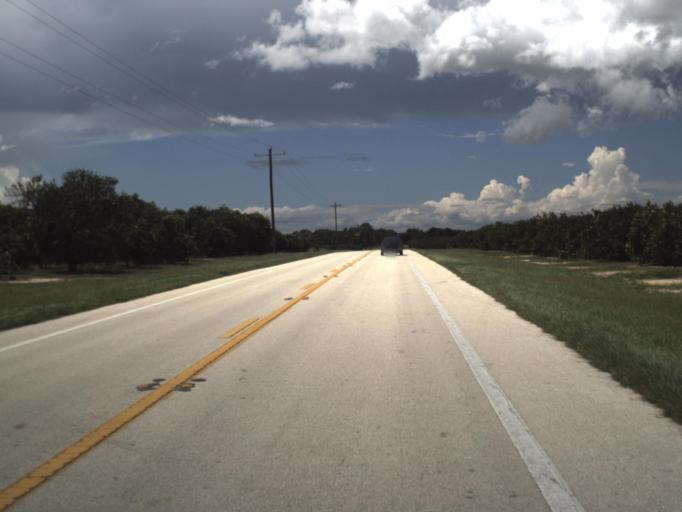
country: US
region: Florida
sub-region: Polk County
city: Fort Meade
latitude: 27.7335
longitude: -81.7178
